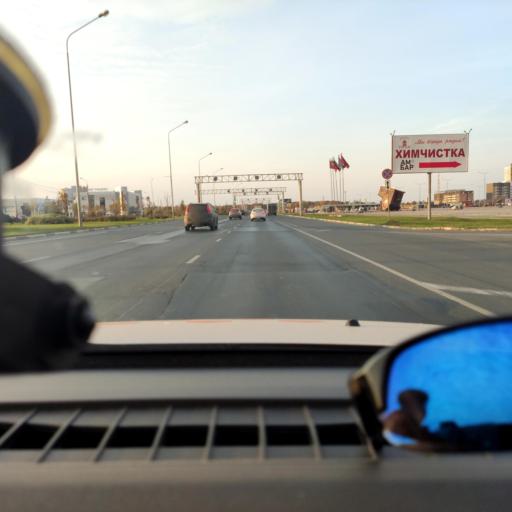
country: RU
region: Samara
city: Samara
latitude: 53.1394
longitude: 50.1770
